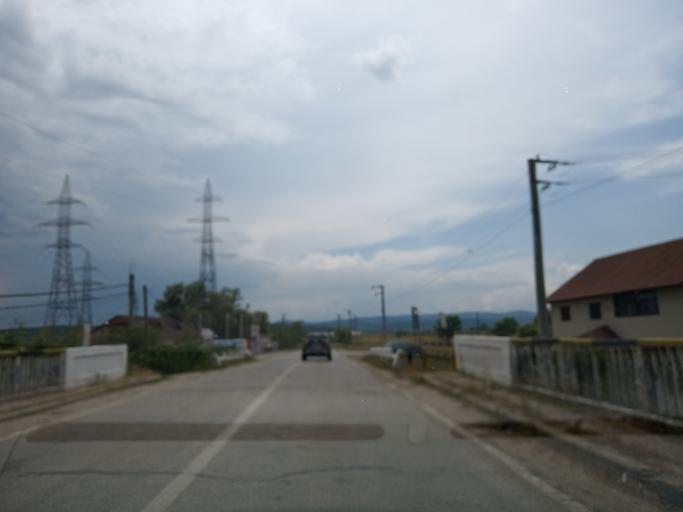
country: RO
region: Gorj
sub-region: Comuna Tismana
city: Tismana
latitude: 45.0355
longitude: 22.9486
